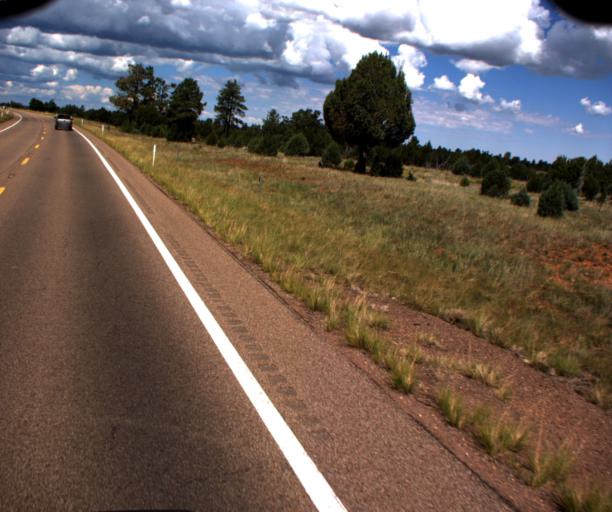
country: US
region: Arizona
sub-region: Navajo County
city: Heber-Overgaard
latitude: 34.3791
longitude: -110.4697
